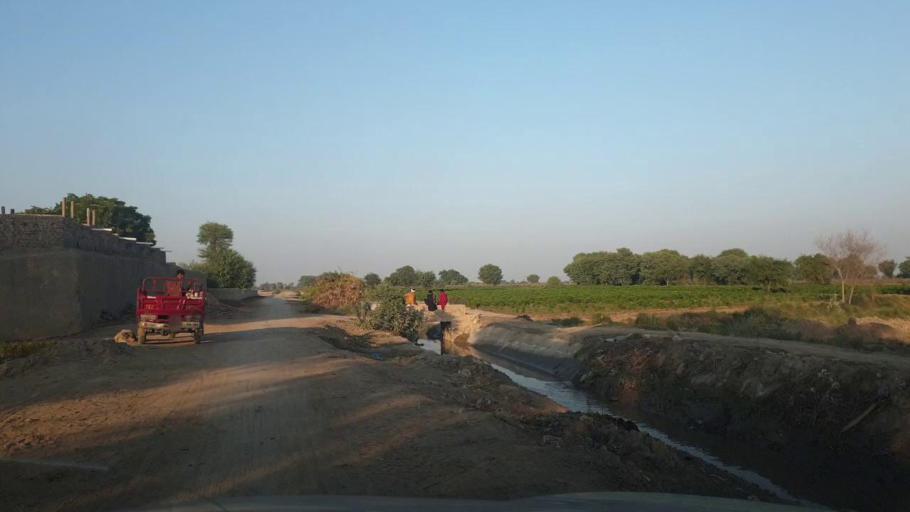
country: PK
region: Sindh
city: Bhan
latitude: 26.5506
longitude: 67.7394
